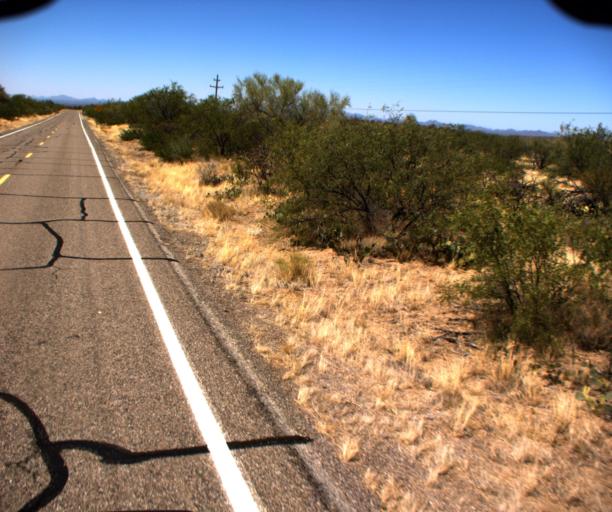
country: US
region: Arizona
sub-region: Pima County
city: Three Points
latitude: 32.0201
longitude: -111.5762
